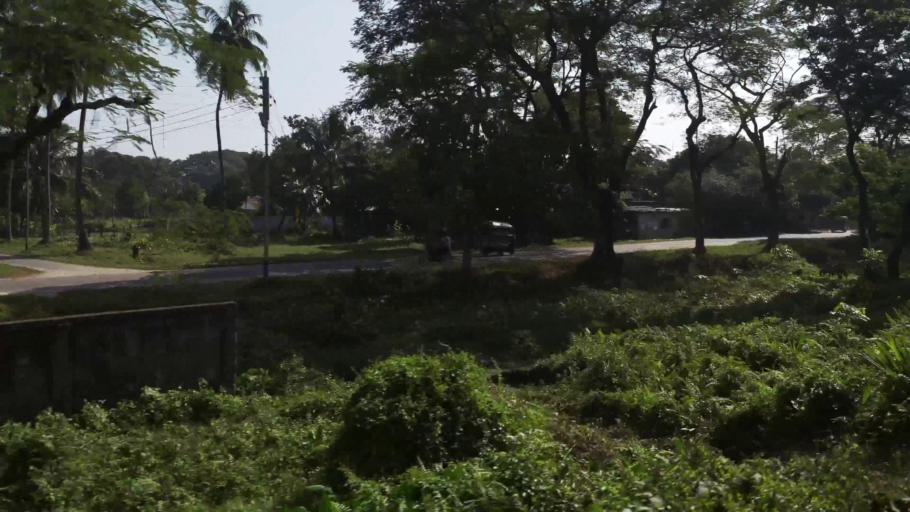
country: BD
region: Dhaka
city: Mymensingh
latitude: 24.6045
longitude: 90.4903
